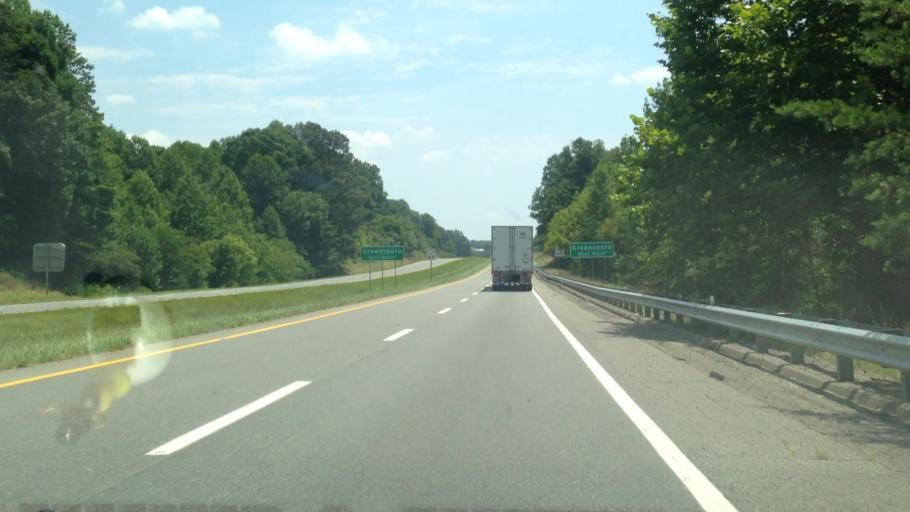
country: US
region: Virginia
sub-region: City of Martinsville
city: Martinsville
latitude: 36.6250
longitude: -79.8717
